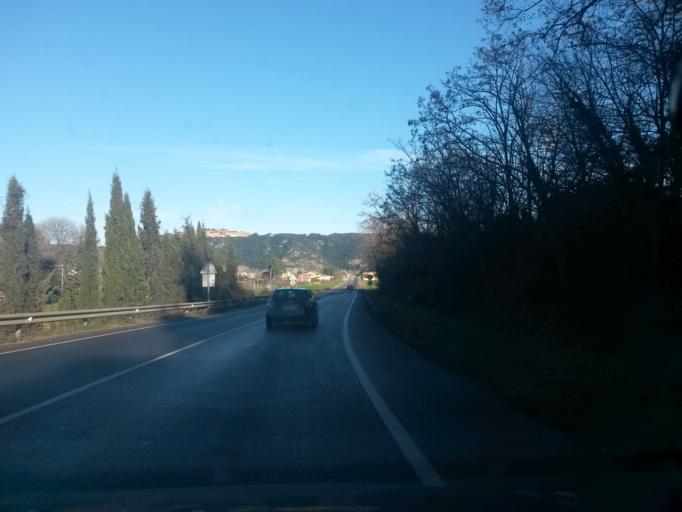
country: ES
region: Catalonia
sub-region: Provincia de Girona
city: Sarria de Ter
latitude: 42.0211
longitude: 2.8317
